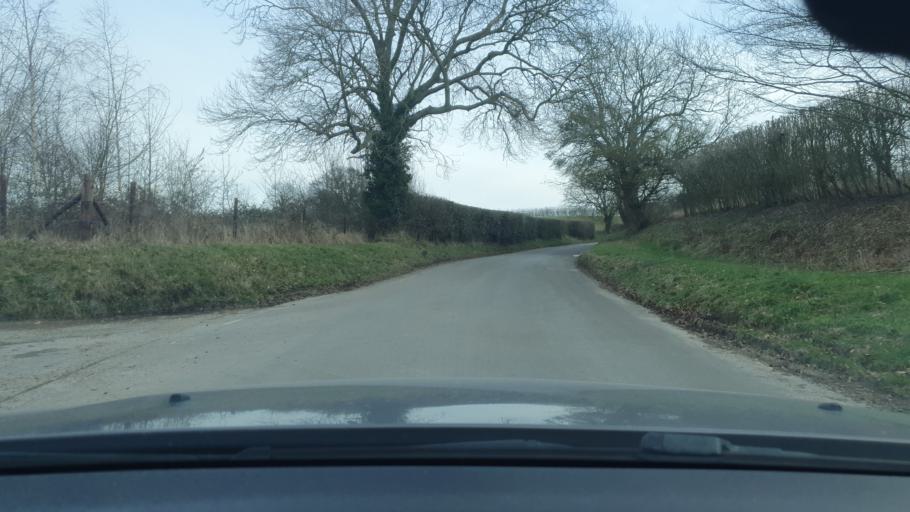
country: GB
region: England
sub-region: West Berkshire
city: Kintbury
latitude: 51.3724
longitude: -1.4759
